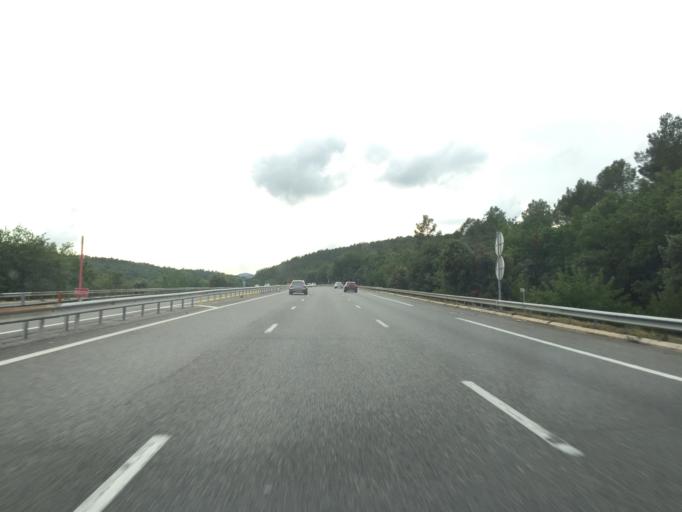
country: FR
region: Provence-Alpes-Cote d'Azur
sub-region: Departement du Var
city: Camps-la-Source
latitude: 43.4119
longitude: 6.1437
